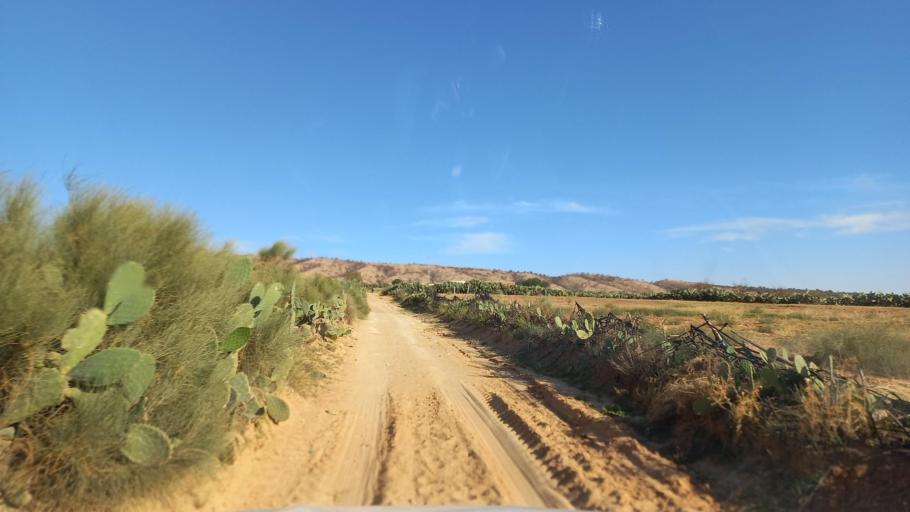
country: TN
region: Al Qasrayn
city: Sbiba
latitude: 35.3300
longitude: 9.1263
